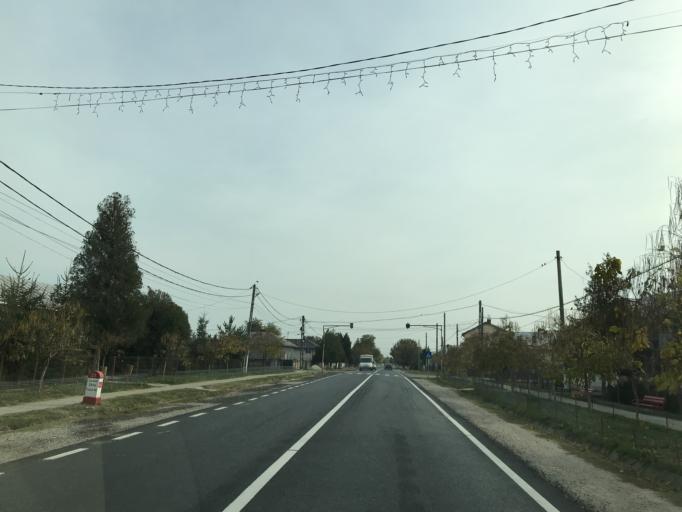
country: RO
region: Olt
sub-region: Comuna Piatra Olt
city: Piatra
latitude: 44.3612
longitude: 24.2940
